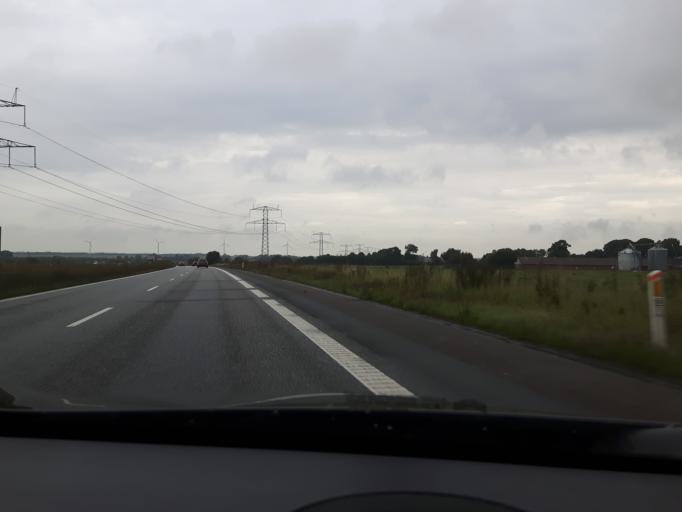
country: DK
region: Central Jutland
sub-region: Randers Kommune
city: Spentrup
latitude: 56.5003
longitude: 9.9776
